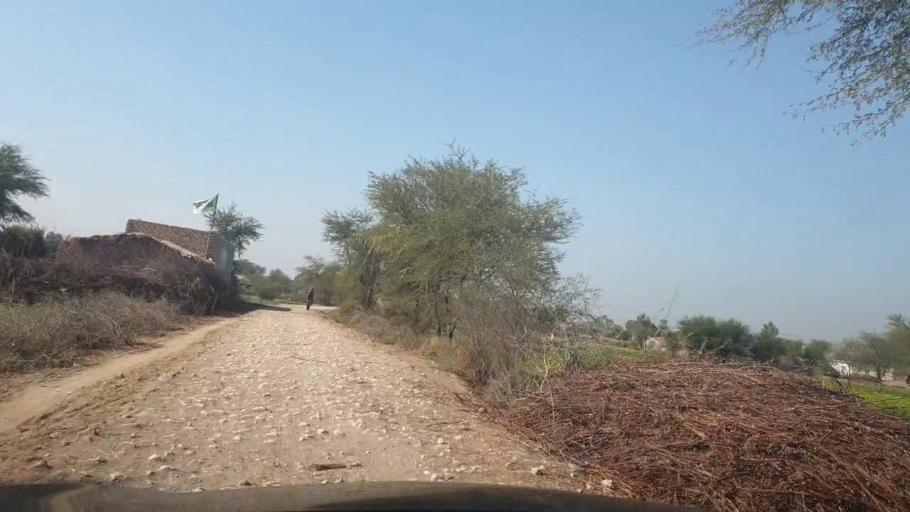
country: PK
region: Sindh
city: Ubauro
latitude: 28.1326
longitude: 69.6768
